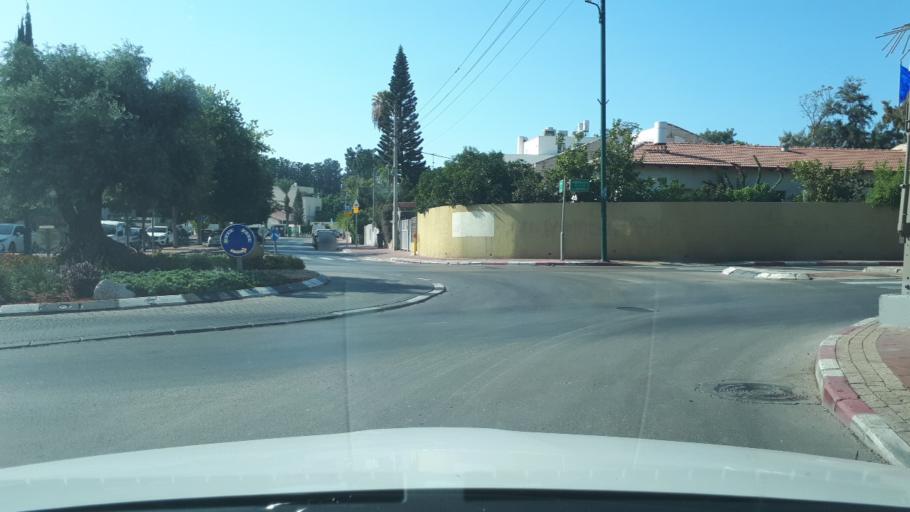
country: IL
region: Tel Aviv
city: Giv`atayim
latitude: 32.0578
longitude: 34.8279
